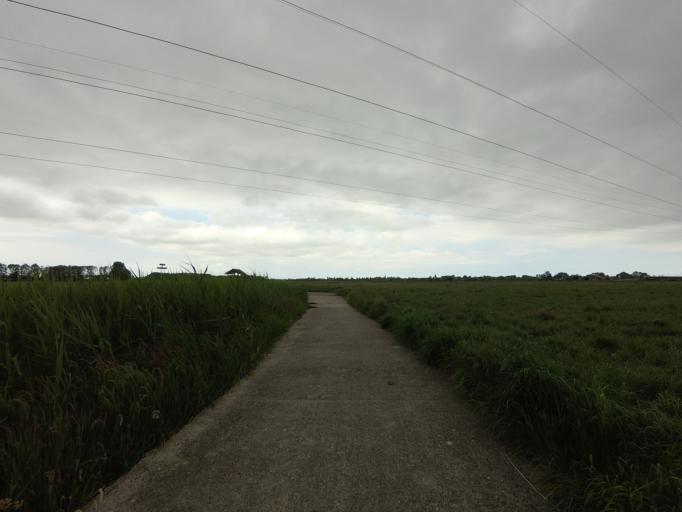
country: NL
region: North Holland
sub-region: Gemeente Hoorn
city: Hoorn
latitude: 52.6641
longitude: 5.0235
